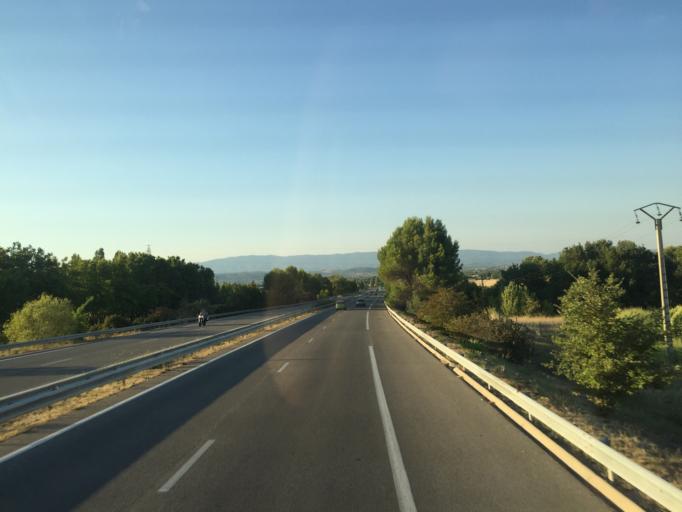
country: FR
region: Provence-Alpes-Cote d'Azur
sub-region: Departement des Bouches-du-Rhone
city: Meyrargues
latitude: 43.6443
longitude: 5.4920
